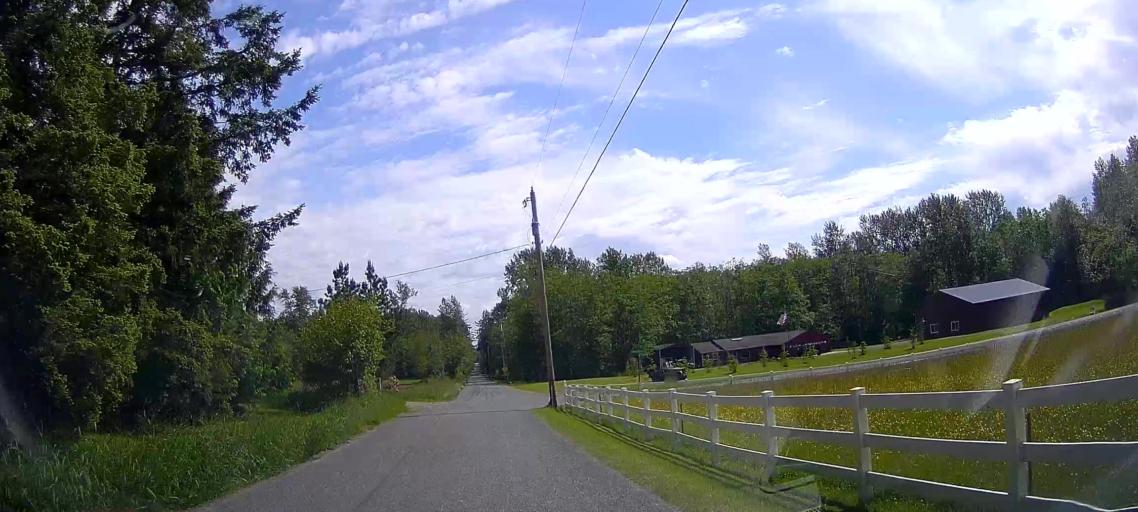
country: US
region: Washington
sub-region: Skagit County
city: Burlington
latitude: 48.5448
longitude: -122.3621
